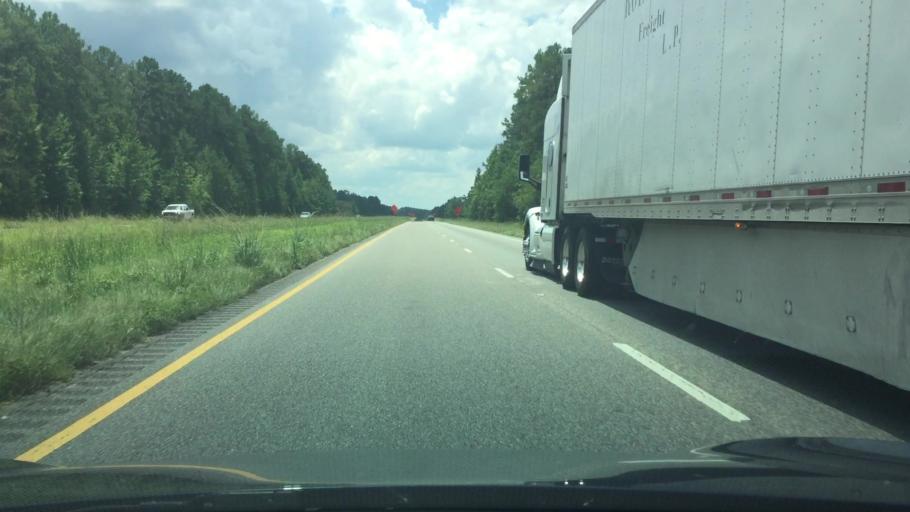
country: US
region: Alabama
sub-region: Pike County
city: Troy
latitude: 31.9888
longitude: -86.0269
